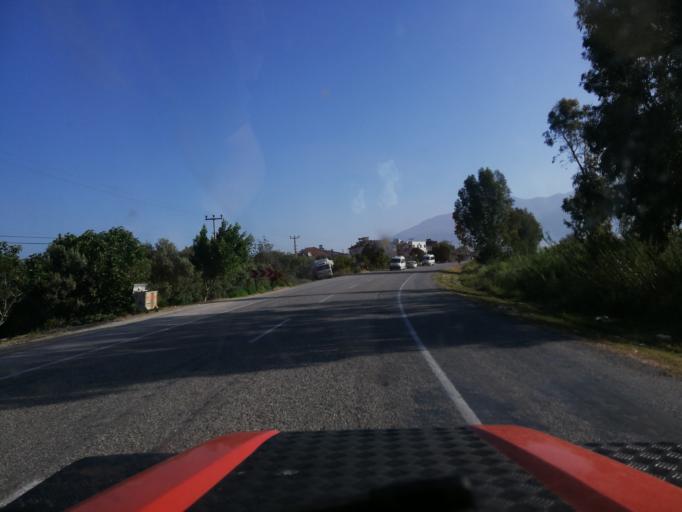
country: TR
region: Antalya
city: Kalkan
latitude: 36.3025
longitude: 29.3272
